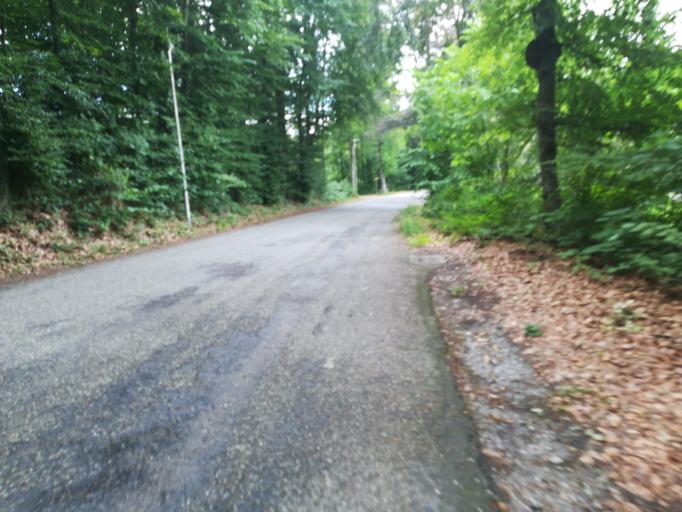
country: CH
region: Thurgau
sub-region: Kreuzlingen District
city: Ermatingen
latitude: 47.6576
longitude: 9.0787
